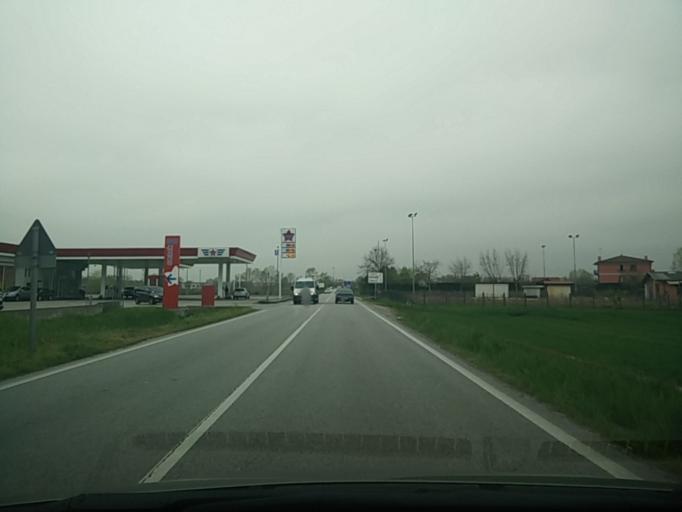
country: IT
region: Veneto
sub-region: Provincia di Venezia
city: Mirano
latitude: 45.4861
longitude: 12.1231
